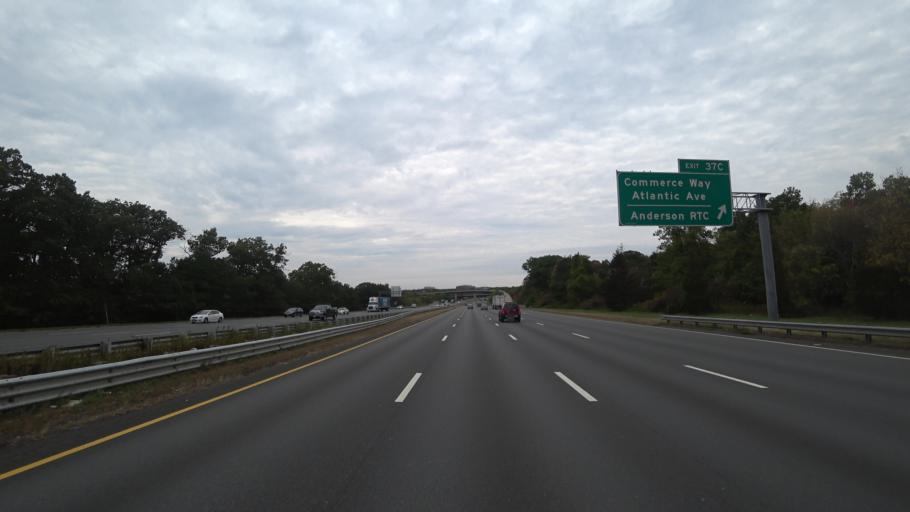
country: US
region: Massachusetts
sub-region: Middlesex County
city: Reading
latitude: 42.5162
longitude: -71.1298
